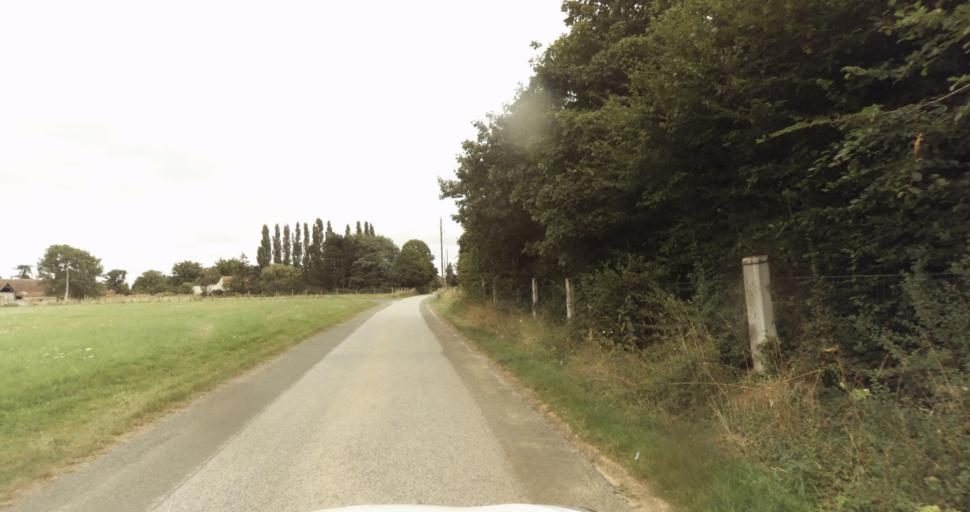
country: FR
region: Haute-Normandie
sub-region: Departement de l'Eure
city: Nonancourt
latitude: 48.8254
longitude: 1.1751
